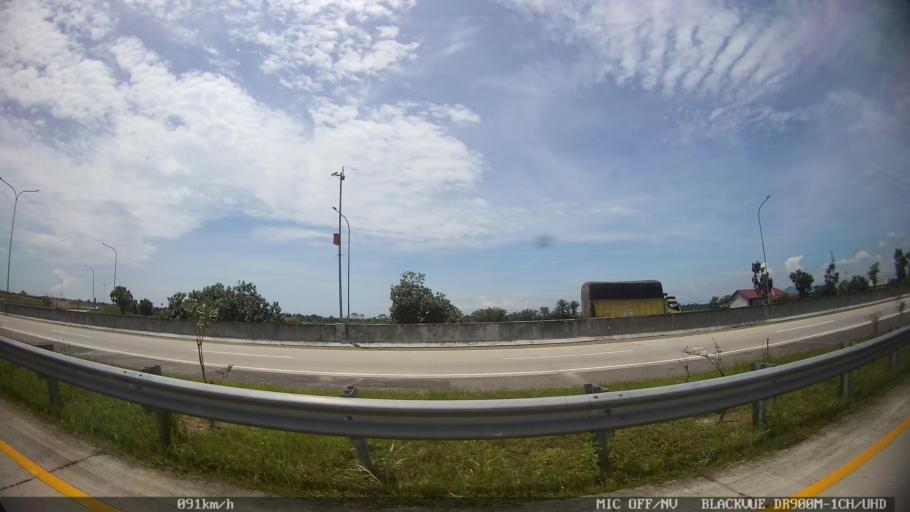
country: ID
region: North Sumatra
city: Perbaungan
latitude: 3.5322
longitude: 98.8903
